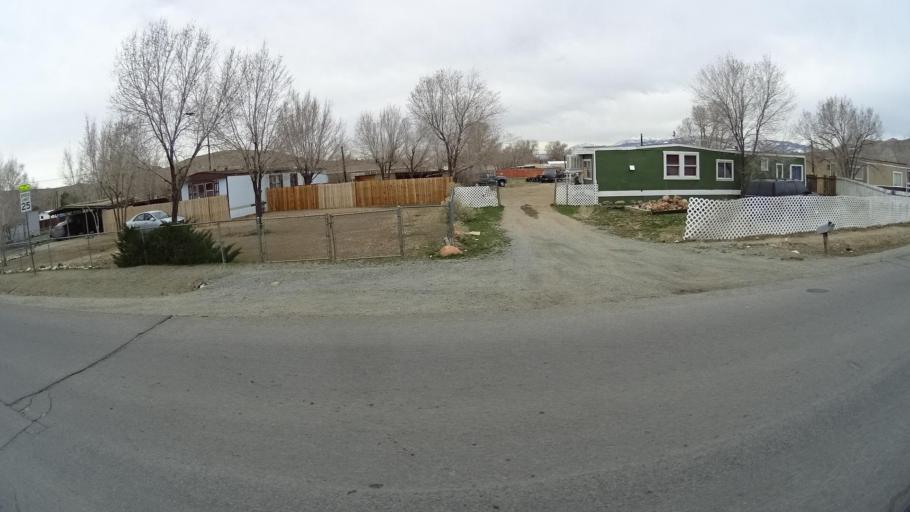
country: US
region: Nevada
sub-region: Washoe County
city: Sun Valley
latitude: 39.5927
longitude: -119.7726
